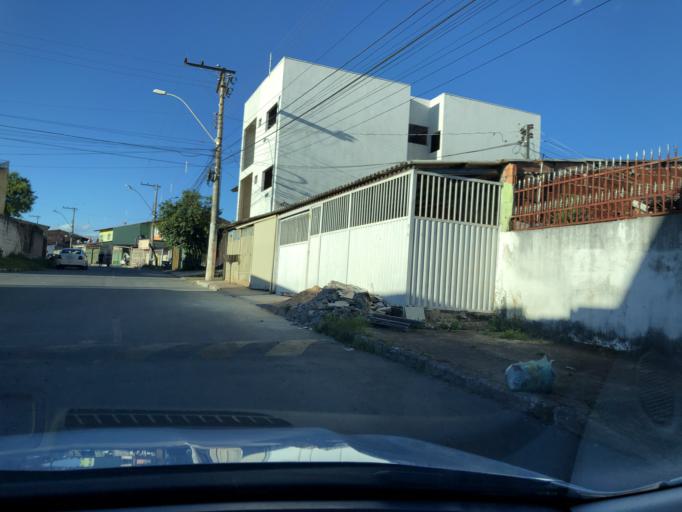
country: BR
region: Federal District
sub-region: Brasilia
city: Brasilia
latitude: -15.7748
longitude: -47.7823
